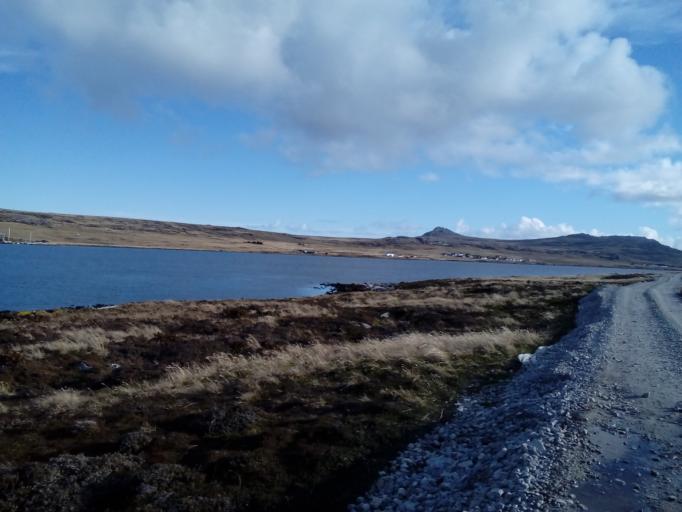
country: FK
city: Stanley
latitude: -51.6836
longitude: -57.8883
